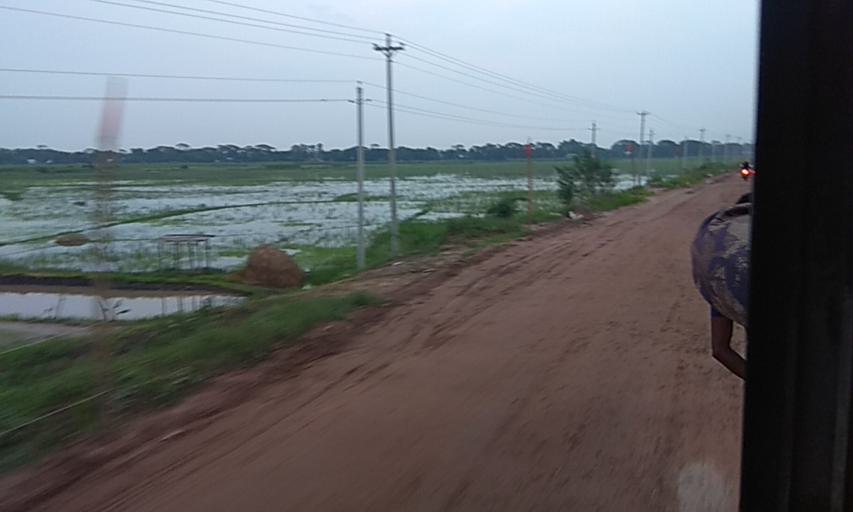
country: BD
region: Dhaka
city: Char Bhadrasan
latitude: 23.3841
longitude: 89.9980
